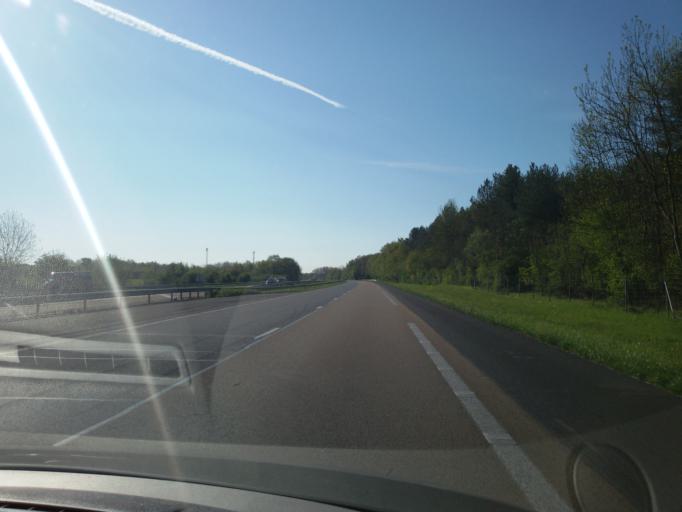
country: FR
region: Bourgogne
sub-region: Departement de l'Yonne
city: Cheroy
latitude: 48.1210
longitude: 2.9743
